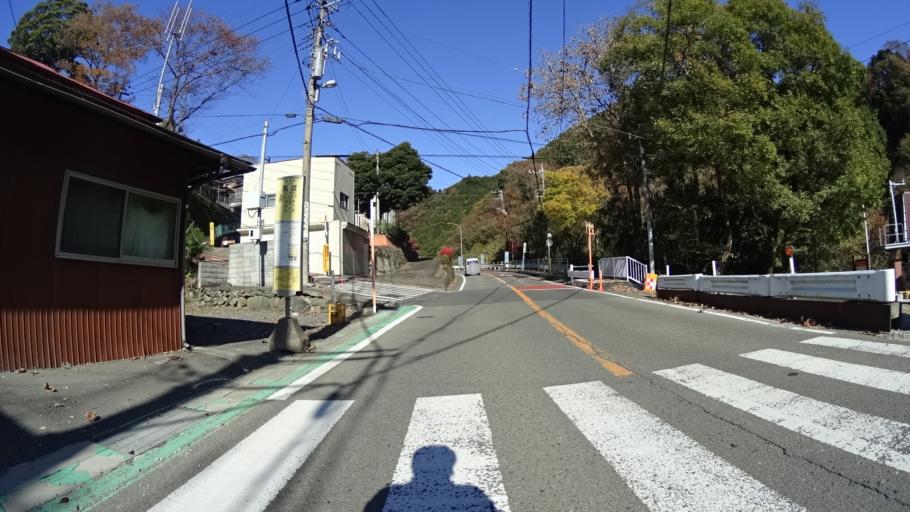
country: JP
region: Kanagawa
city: Zama
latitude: 35.5322
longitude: 139.2849
